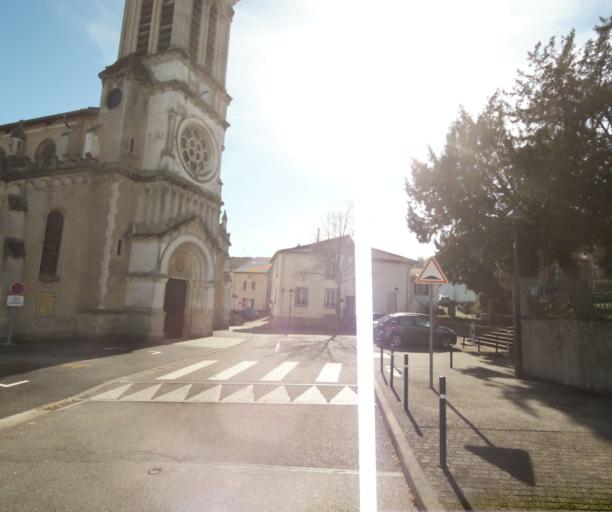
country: FR
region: Lorraine
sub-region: Departement de Meurthe-et-Moselle
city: Villers-les-Nancy
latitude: 48.6692
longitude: 6.1449
